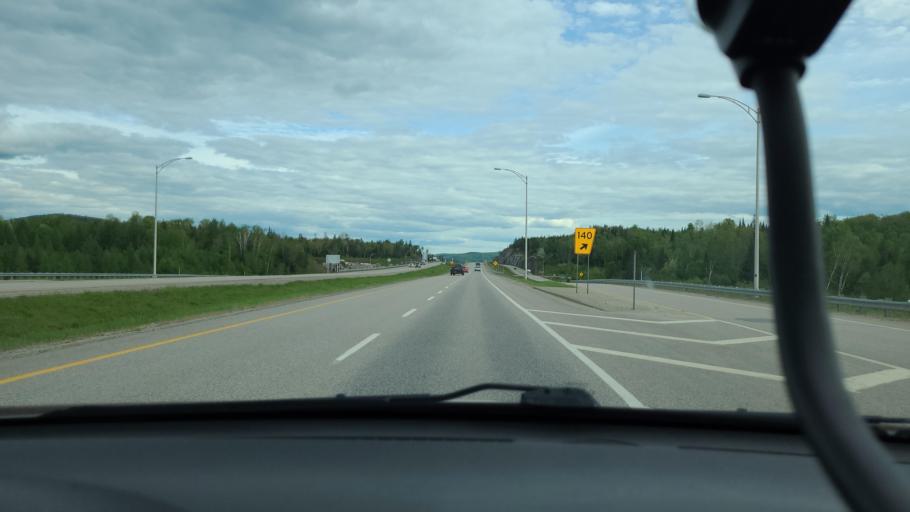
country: CA
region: Quebec
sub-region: Laurentides
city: Labelle
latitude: 46.2602
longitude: -74.7271
